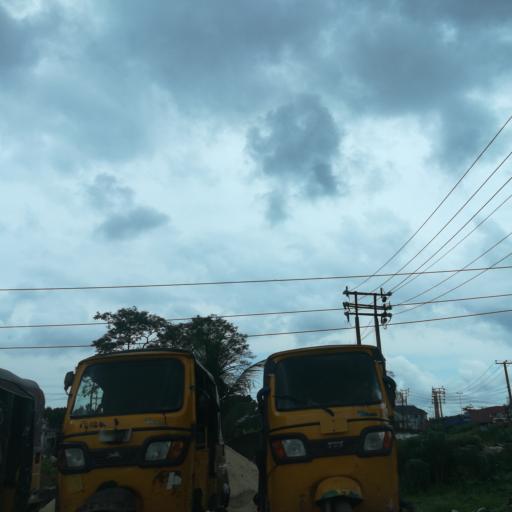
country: NG
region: Rivers
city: Port Harcourt
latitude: 4.8282
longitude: 7.0362
